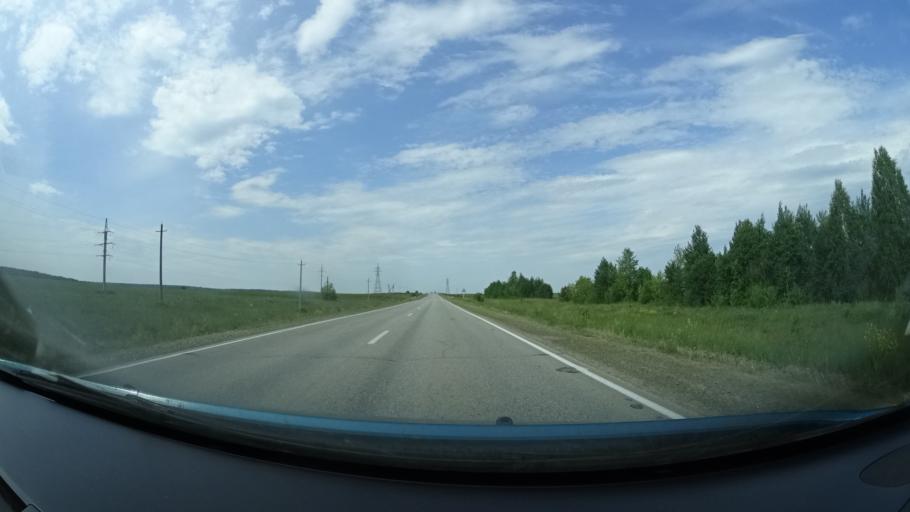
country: RU
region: Perm
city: Barda
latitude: 57.0033
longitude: 55.5661
